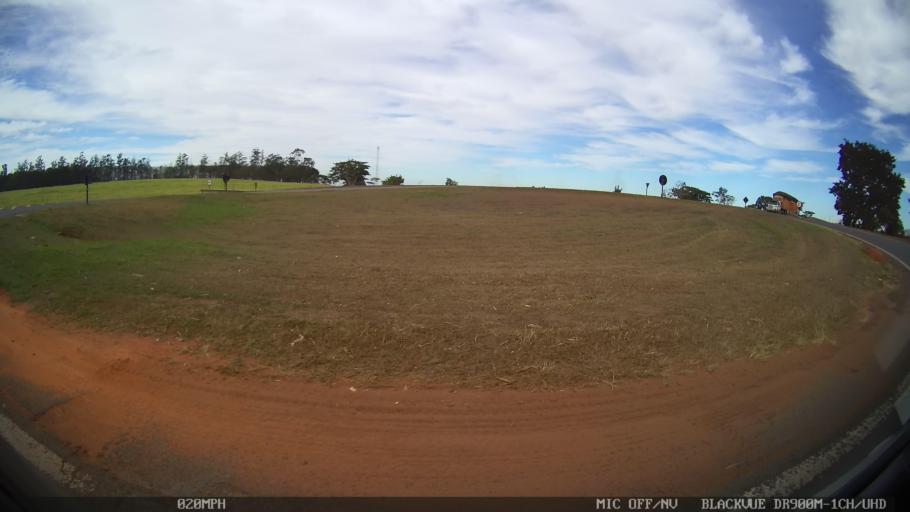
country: BR
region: Sao Paulo
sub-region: Santa Adelia
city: Santa Adelia
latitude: -21.2759
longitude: -48.8605
